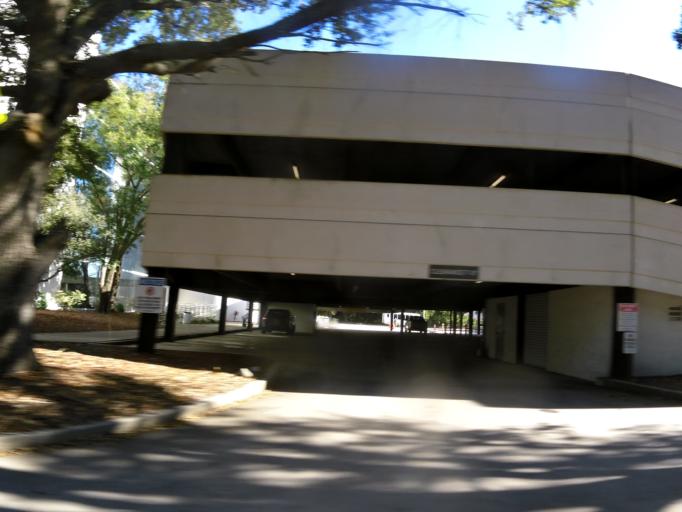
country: US
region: Florida
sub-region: Duval County
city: Jacksonville
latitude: 30.2555
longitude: -81.5884
